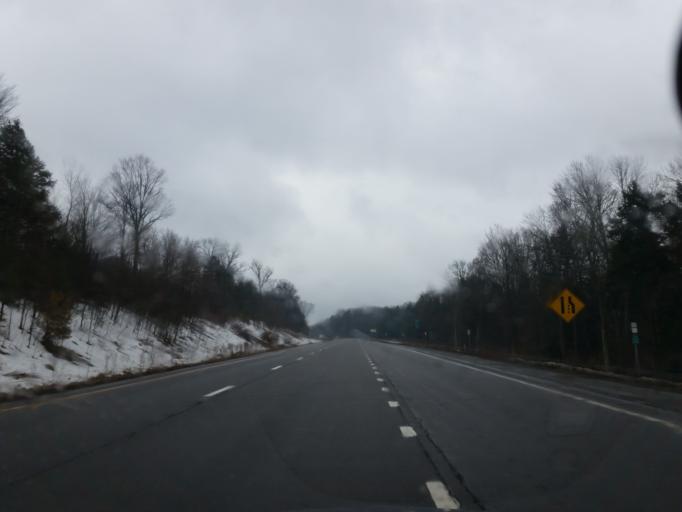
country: US
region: New York
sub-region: Chenango County
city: Lakeview
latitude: 42.3702
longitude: -75.9949
